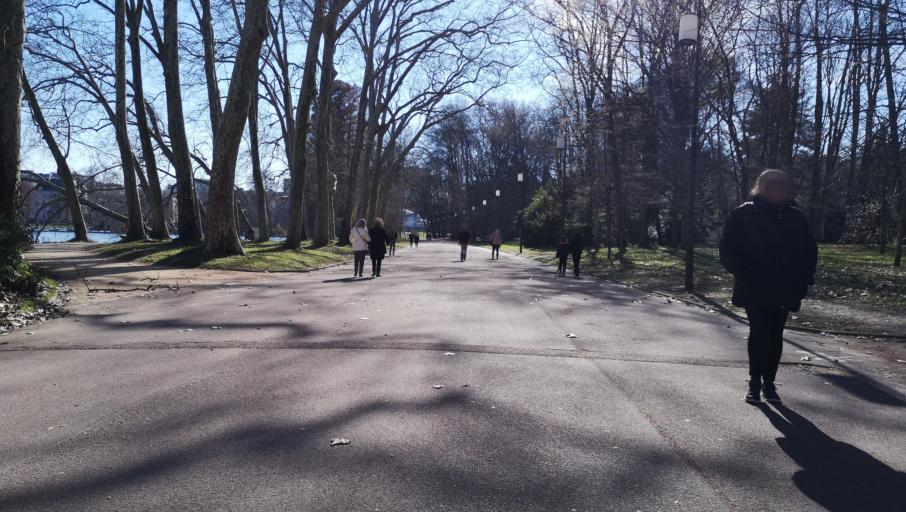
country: FR
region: Rhone-Alpes
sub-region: Departement du Rhone
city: Caluire-et-Cuire
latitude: 45.7802
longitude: 4.8488
